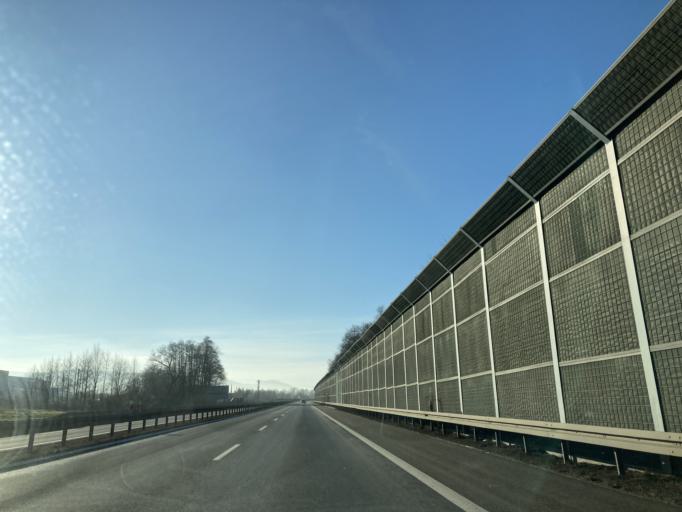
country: PL
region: Silesian Voivodeship
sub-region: Powiat bielski
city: Jaworze
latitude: 49.8239
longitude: 18.9633
